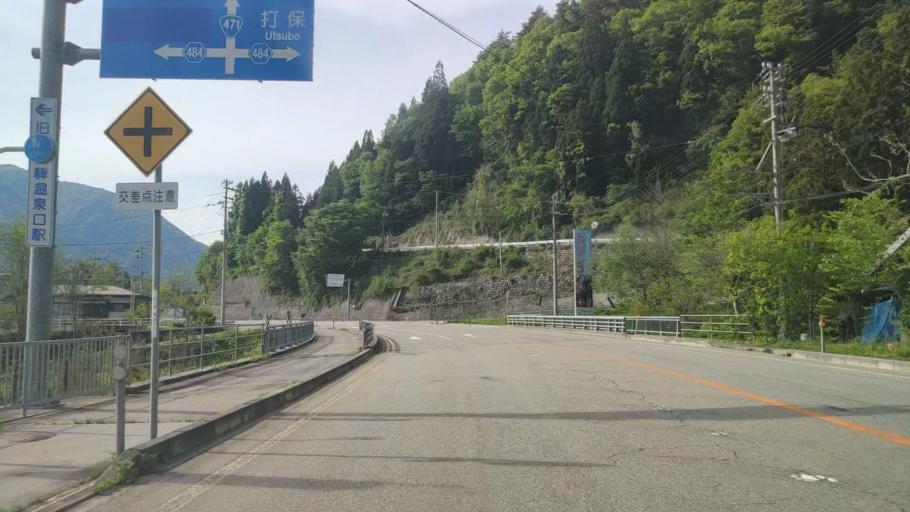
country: JP
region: Gifu
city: Takayama
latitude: 36.3190
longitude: 137.3139
